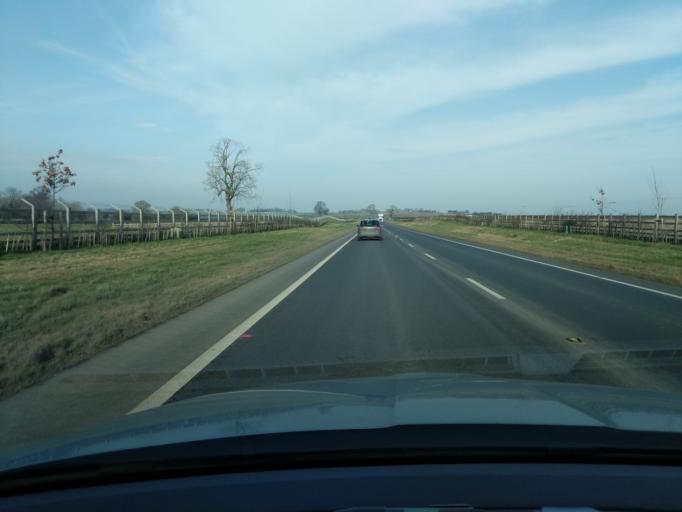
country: GB
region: England
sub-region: North Yorkshire
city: Bedale
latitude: 54.3029
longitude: -1.5850
